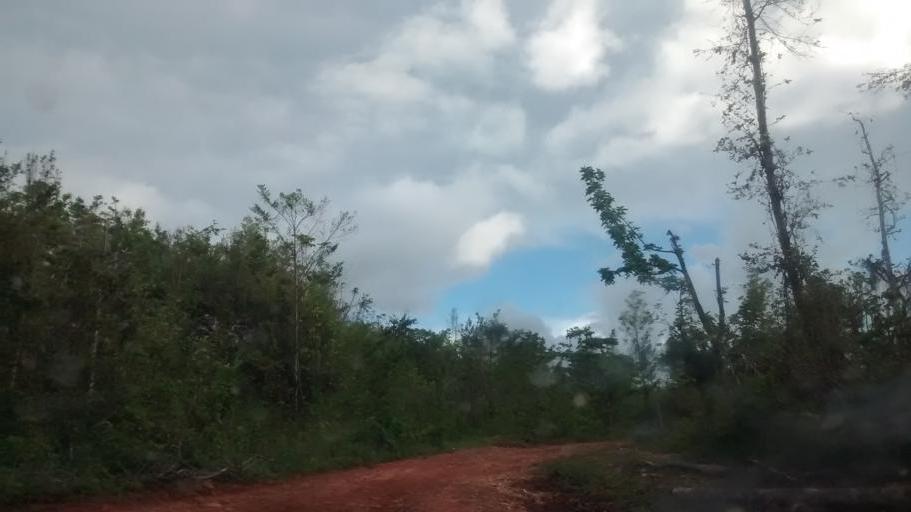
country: HT
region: Grandans
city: Corail
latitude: 18.5074
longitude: -73.7817
